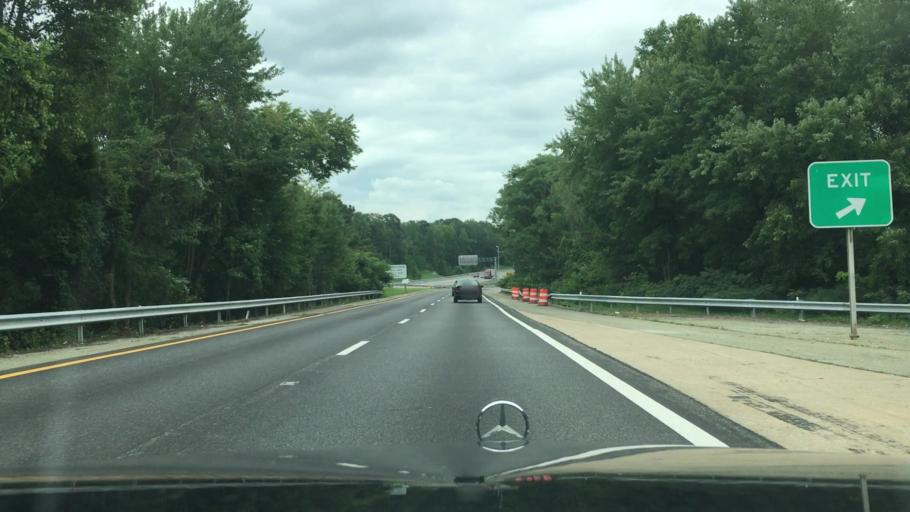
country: US
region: Virginia
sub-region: Chesterfield County
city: Bon Air
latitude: 37.5263
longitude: -77.5276
